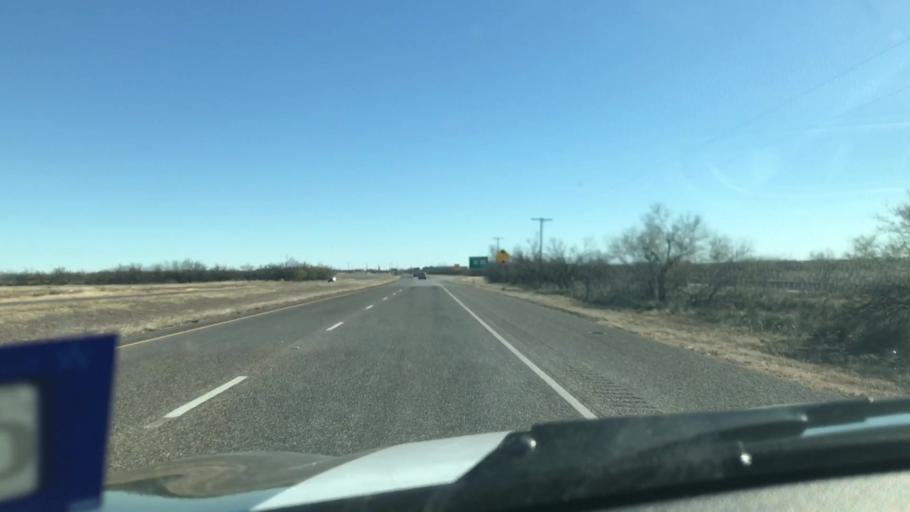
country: US
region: Texas
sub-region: Scurry County
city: Snyder
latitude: 32.8004
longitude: -100.9666
